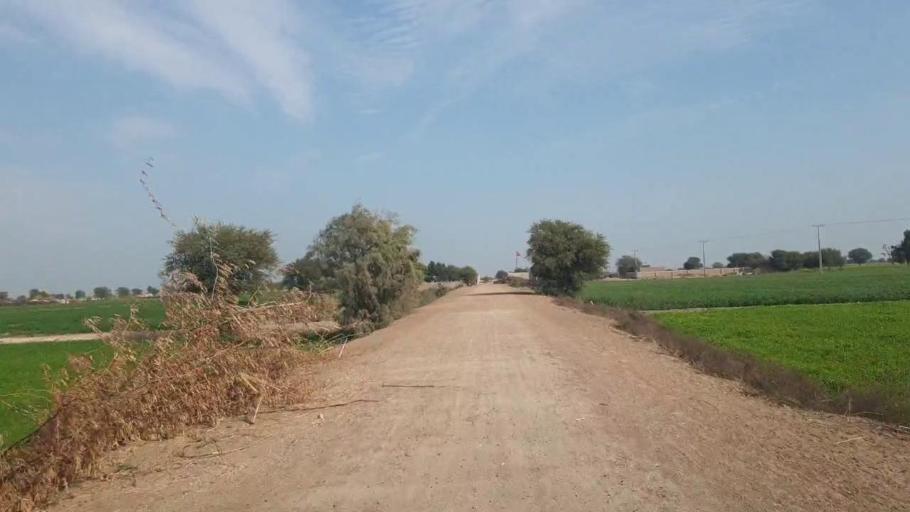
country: PK
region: Sindh
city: Shahdadpur
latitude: 26.0151
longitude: 68.5514
